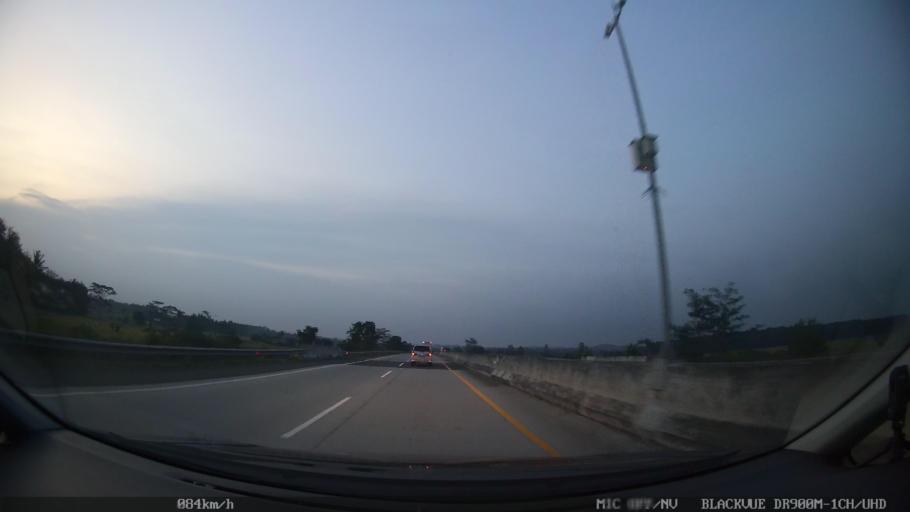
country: ID
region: Lampung
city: Sidorejo
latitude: -5.5856
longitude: 105.5446
